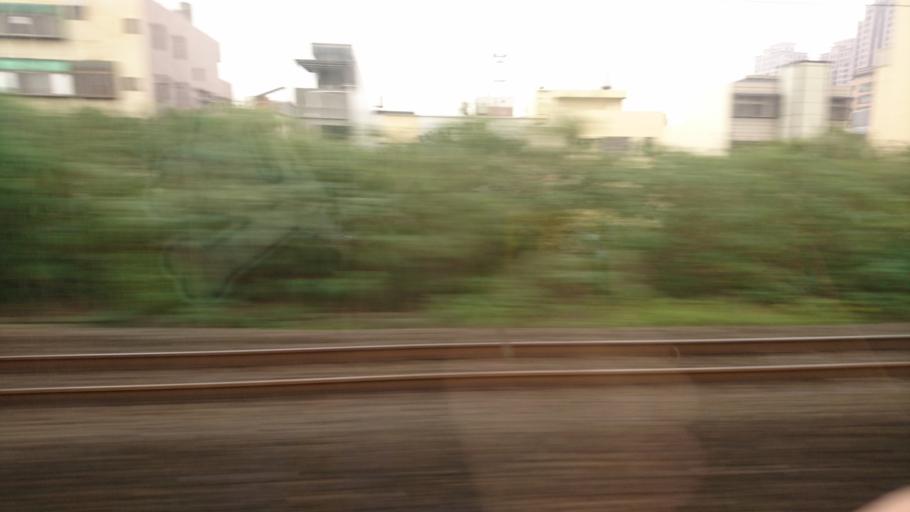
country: TW
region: Taiwan
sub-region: Hsinchu
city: Zhubei
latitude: 24.8297
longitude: 121.0023
